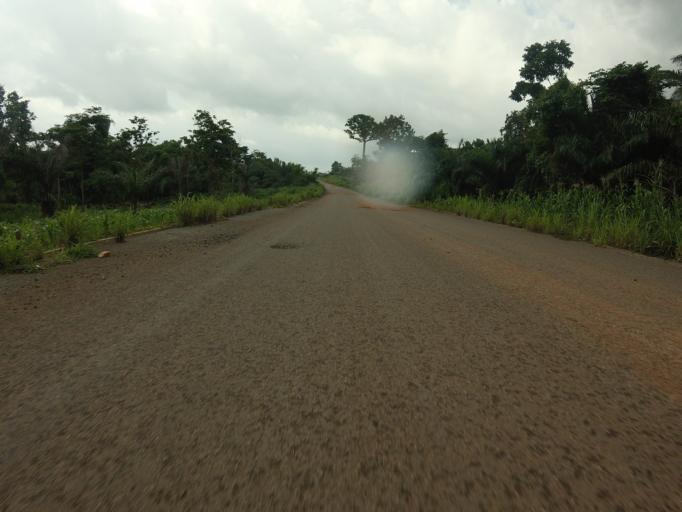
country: TG
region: Plateaux
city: Kpalime
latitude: 6.9247
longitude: 0.4615
